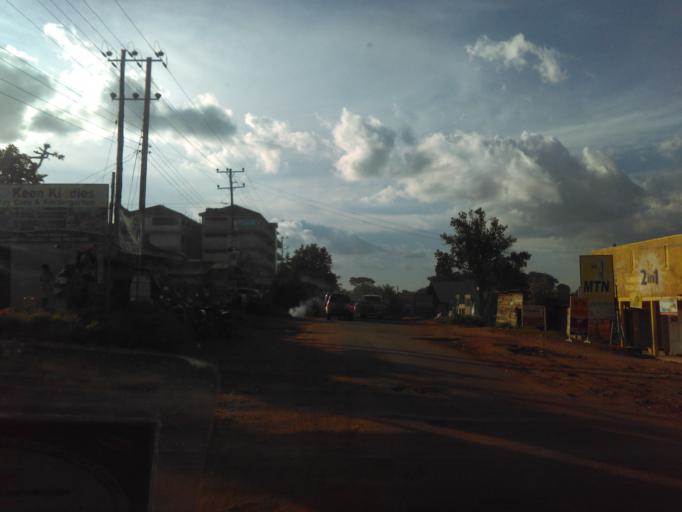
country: UG
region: Central Region
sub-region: Wakiso District
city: Kajansi
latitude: 0.2577
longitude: 32.5600
